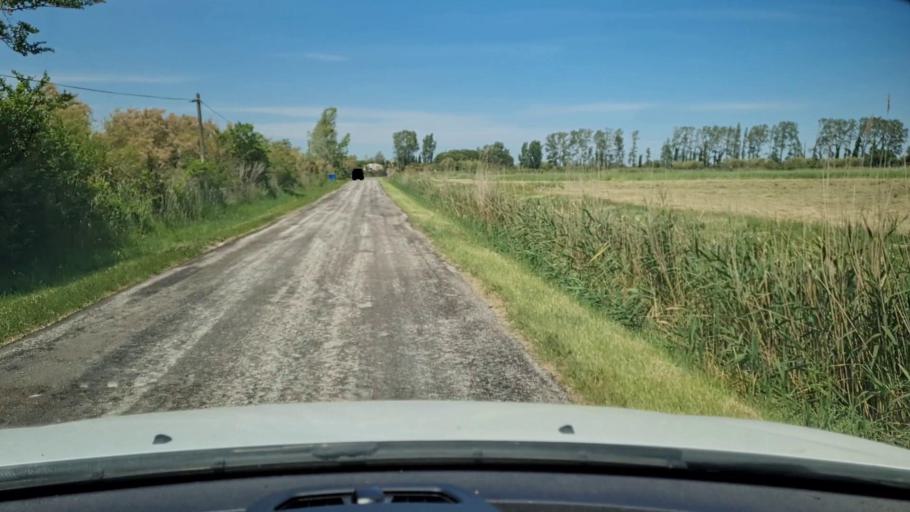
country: FR
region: Provence-Alpes-Cote d'Azur
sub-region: Departement des Bouches-du-Rhone
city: Saintes-Maries-de-la-Mer
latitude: 43.5592
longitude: 4.3822
